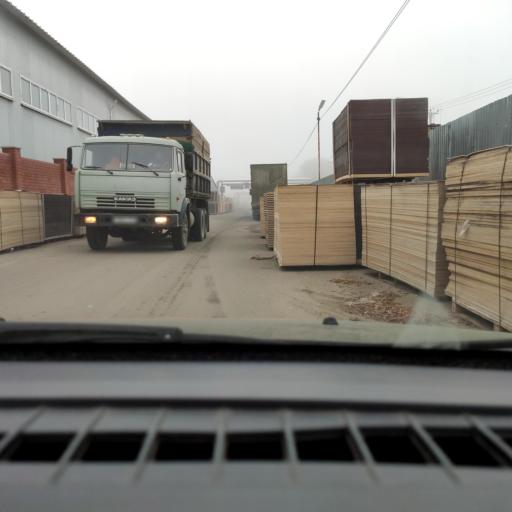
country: RU
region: Samara
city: Tol'yatti
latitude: 53.5742
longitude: 49.2834
